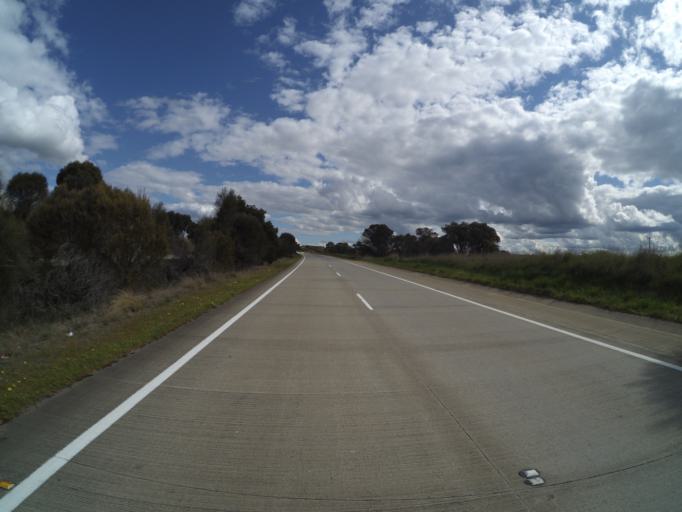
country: AU
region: New South Wales
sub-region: Yass Valley
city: Murrumbateman
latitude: -34.7888
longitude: 149.1756
